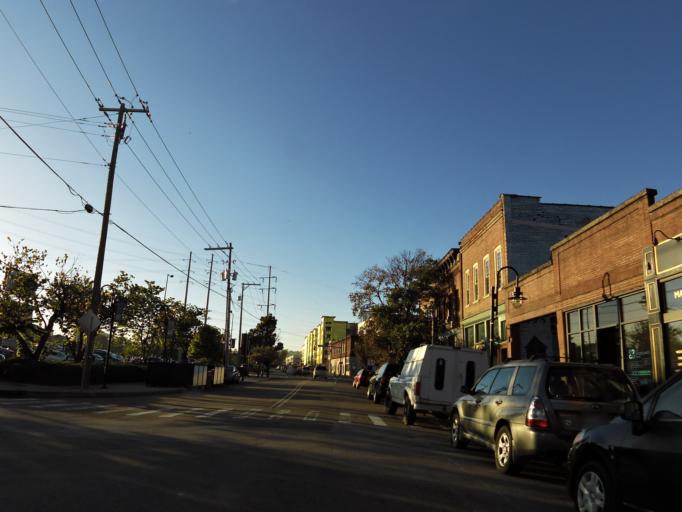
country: US
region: Tennessee
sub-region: Knox County
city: Knoxville
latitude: 35.9696
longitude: -83.9182
